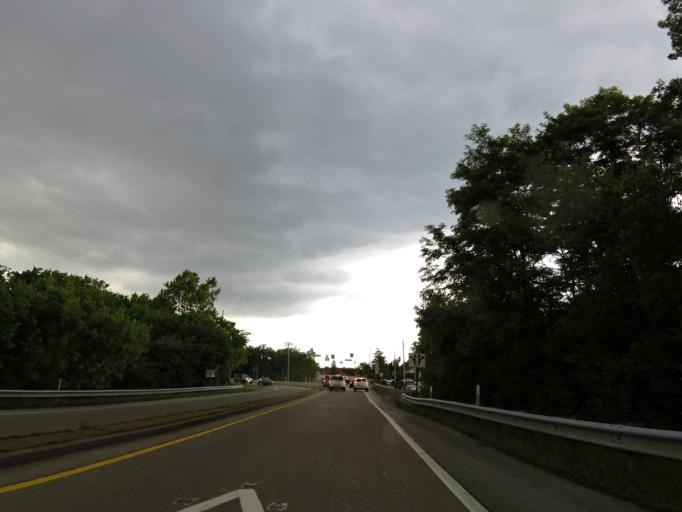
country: US
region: Tennessee
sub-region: Knox County
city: Farragut
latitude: 35.9025
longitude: -84.1165
